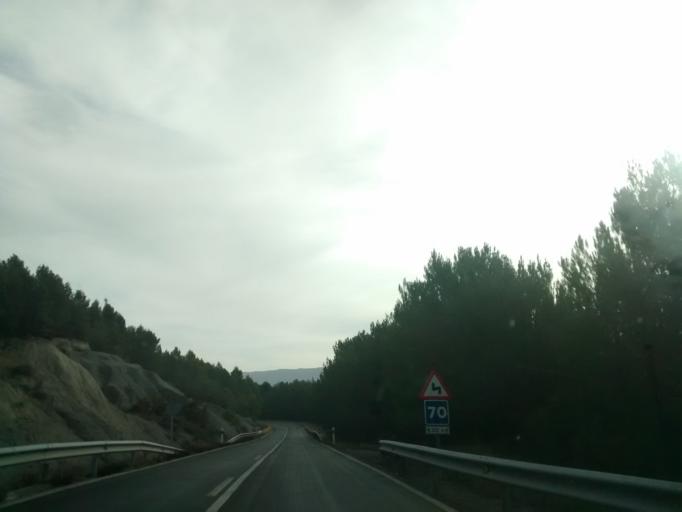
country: ES
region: Aragon
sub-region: Provincia de Zaragoza
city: Siguees
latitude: 42.6147
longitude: -1.0826
